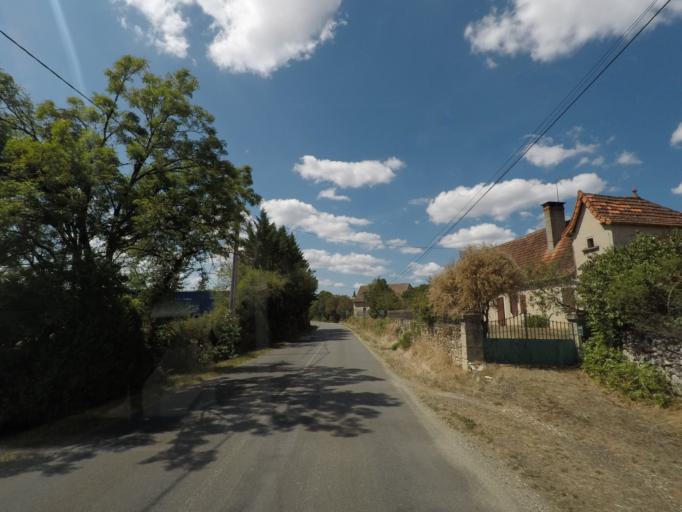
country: FR
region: Midi-Pyrenees
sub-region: Departement du Lot
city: Lacapelle-Marival
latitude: 44.6271
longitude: 1.8252
